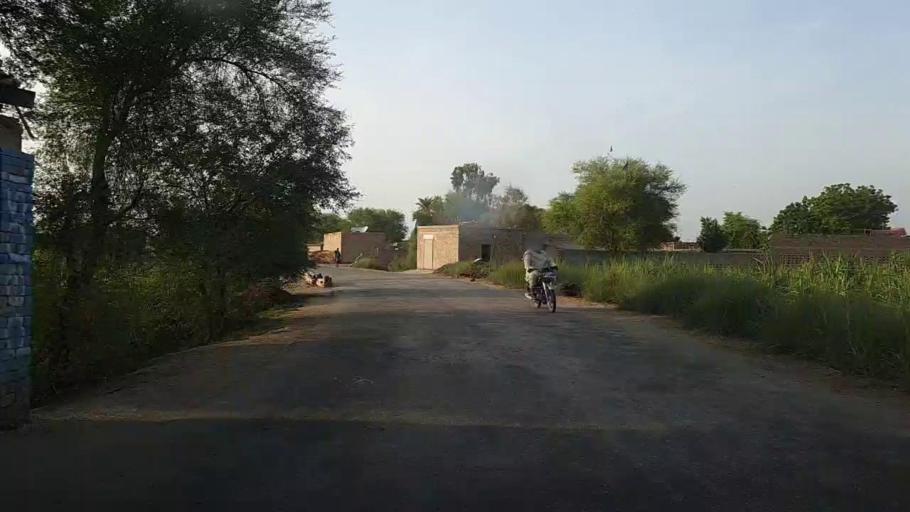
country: PK
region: Sindh
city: Ubauro
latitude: 28.1770
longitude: 69.8294
